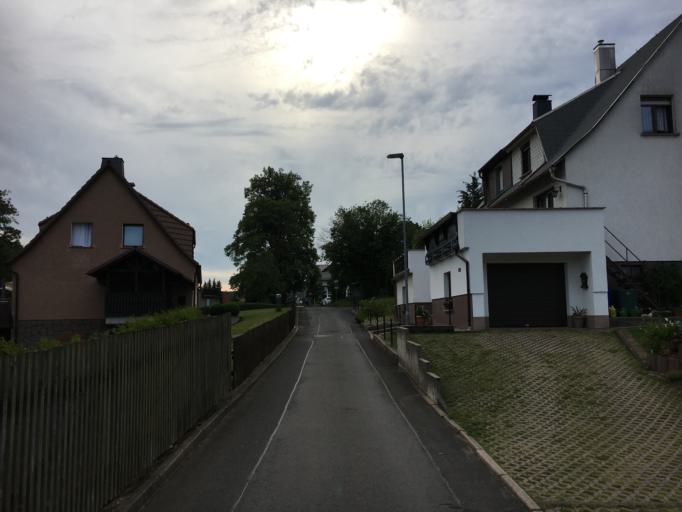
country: DE
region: Thuringia
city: Brotterode
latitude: 50.8264
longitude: 10.4541
